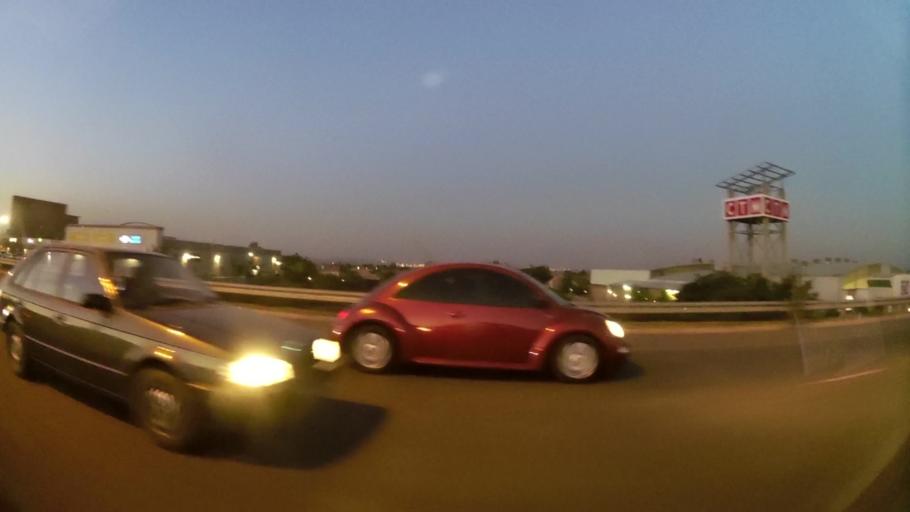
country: ZA
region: North-West
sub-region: Bojanala Platinum District Municipality
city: Rustenburg
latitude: -25.6969
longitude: 27.2541
